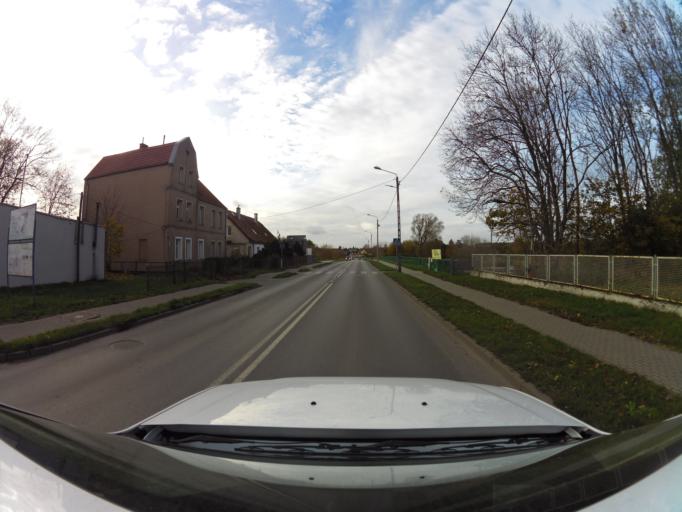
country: PL
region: West Pomeranian Voivodeship
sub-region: Powiat gryficki
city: Gryfice
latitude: 53.9200
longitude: 15.1926
